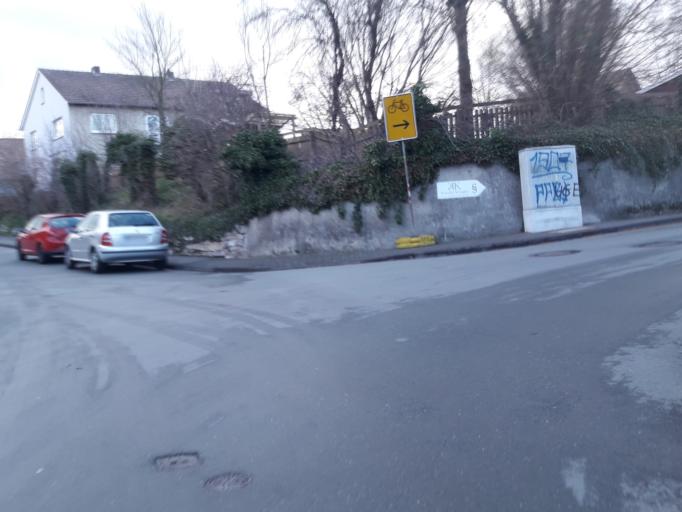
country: DE
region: North Rhine-Westphalia
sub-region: Regierungsbezirk Detmold
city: Paderborn
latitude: 51.6881
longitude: 8.6938
